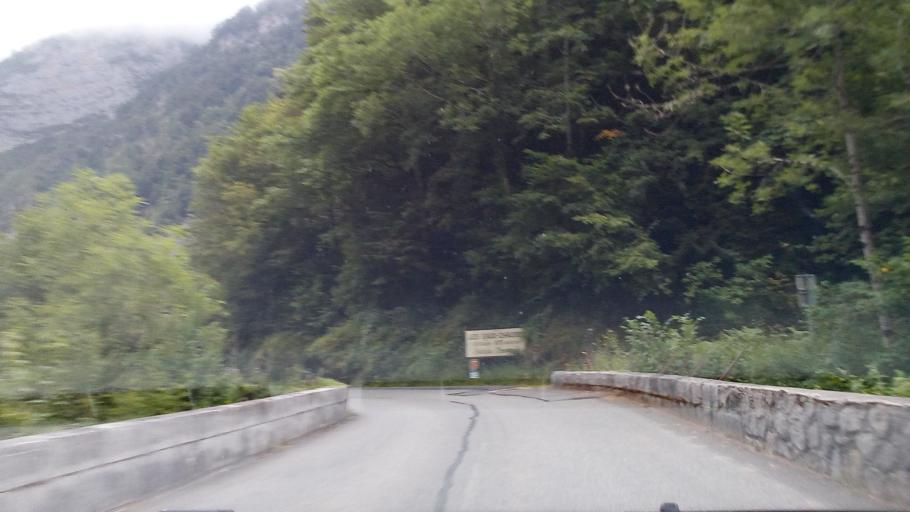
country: FR
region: Aquitaine
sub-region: Departement des Pyrenees-Atlantiques
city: Laruns
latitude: 42.9495
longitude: -0.4432
